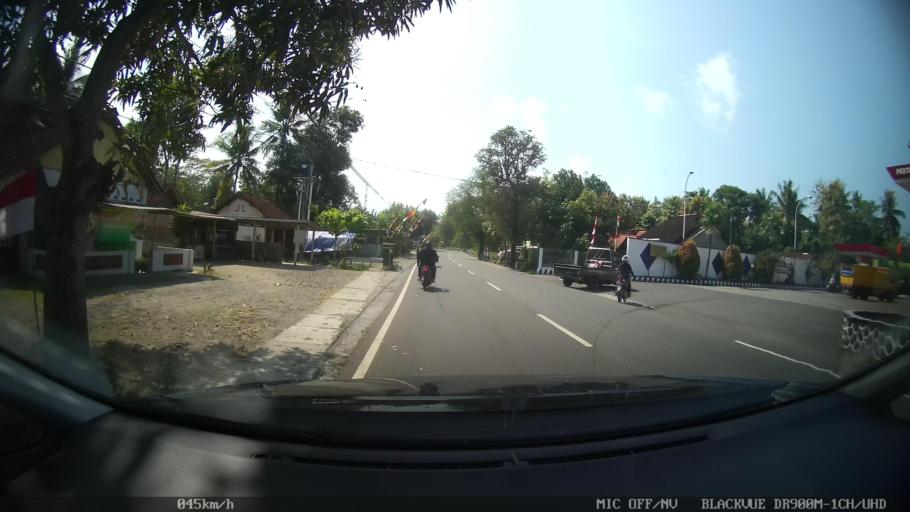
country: ID
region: Daerah Istimewa Yogyakarta
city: Srandakan
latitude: -7.9400
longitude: 110.2278
